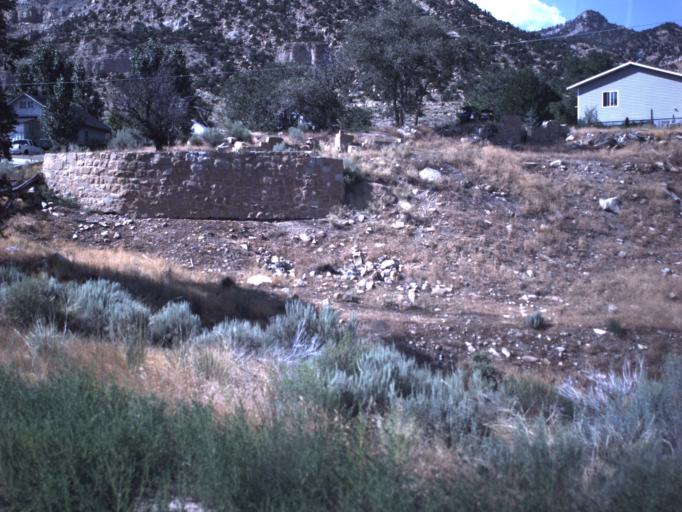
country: US
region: Utah
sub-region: Carbon County
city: Helper
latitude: 39.6882
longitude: -110.8050
